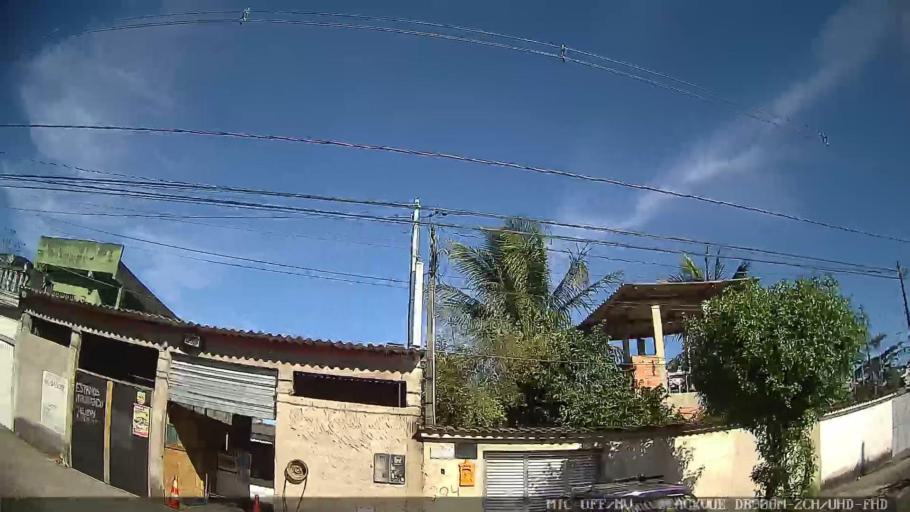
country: BR
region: Sao Paulo
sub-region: Santos
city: Santos
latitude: -23.9432
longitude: -46.2815
